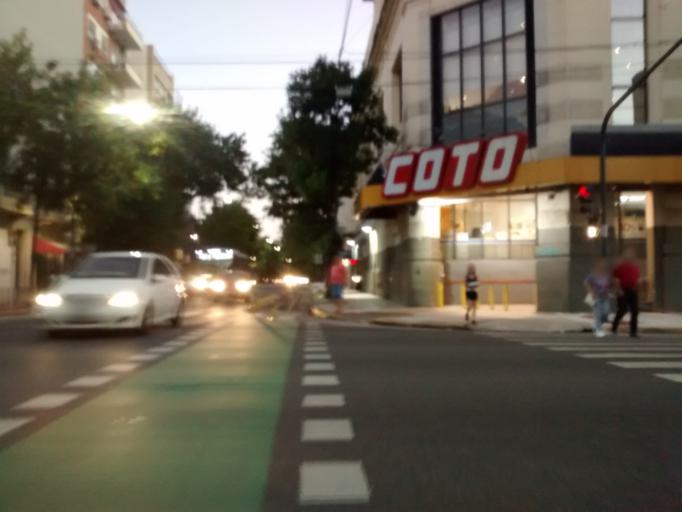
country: AR
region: Buenos Aires F.D.
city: Villa Santa Rita
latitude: -34.6119
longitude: -58.4549
